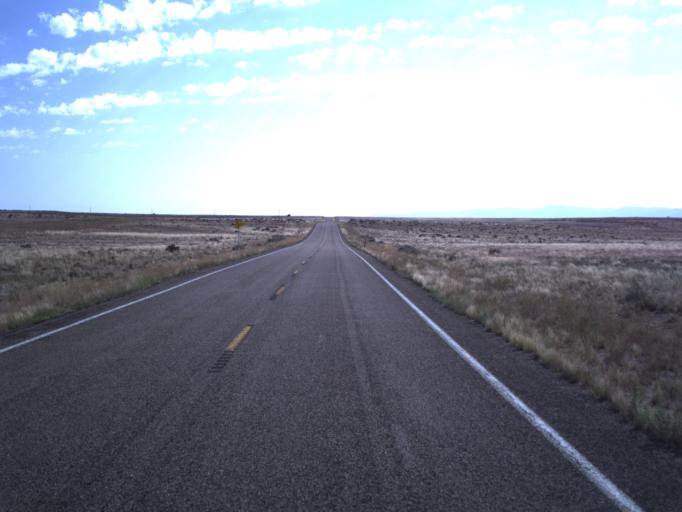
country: US
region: Utah
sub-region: Beaver County
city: Milford
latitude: 38.7971
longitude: -112.8979
